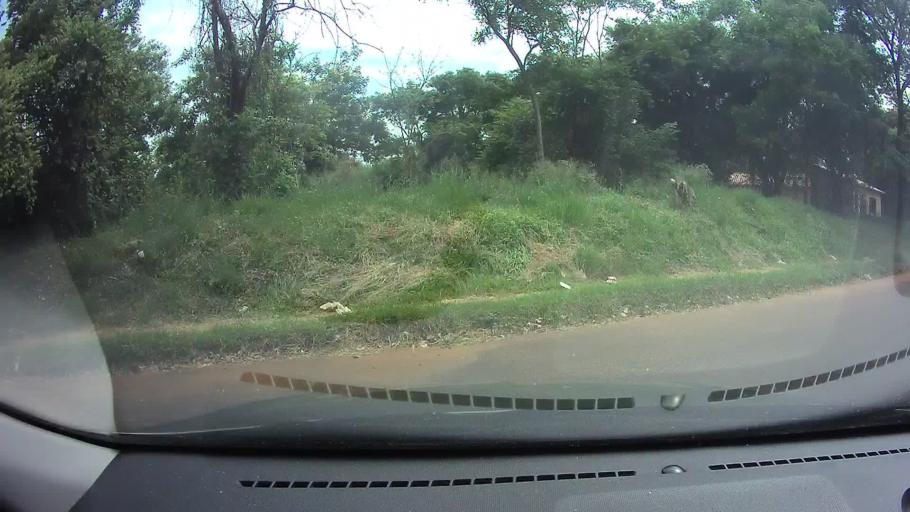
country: PY
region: Central
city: San Lorenzo
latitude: -25.2914
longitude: -57.5062
